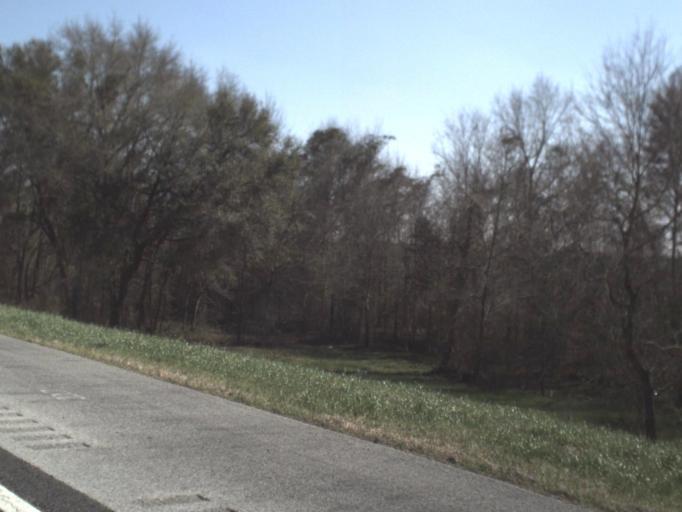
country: US
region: Florida
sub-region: Jackson County
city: Marianna
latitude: 30.6847
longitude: -85.1071
